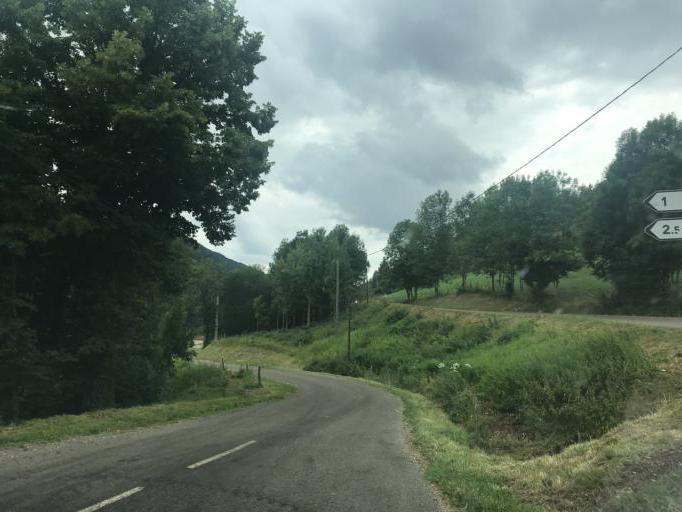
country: FR
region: Franche-Comte
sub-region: Departement du Jura
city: Saint-Claude
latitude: 46.3510
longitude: 5.8393
